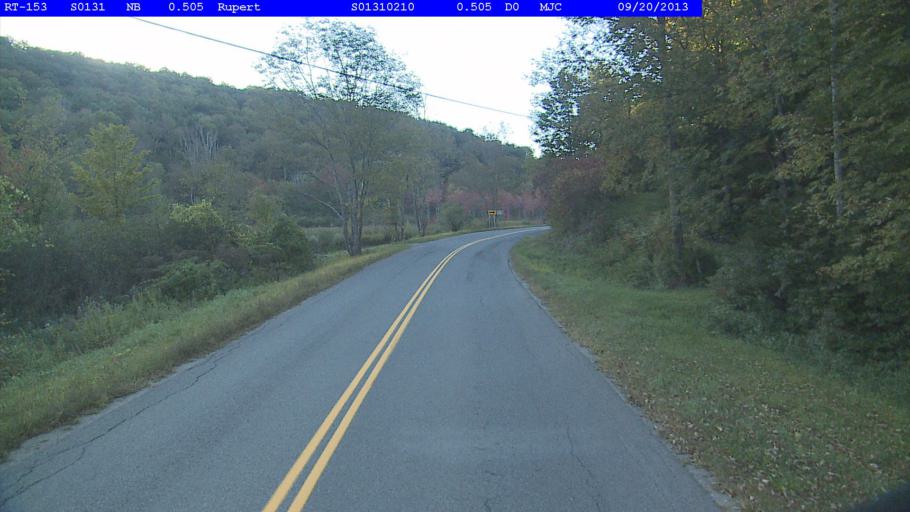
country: US
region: New York
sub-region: Washington County
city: Granville
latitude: 43.2640
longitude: -73.2308
